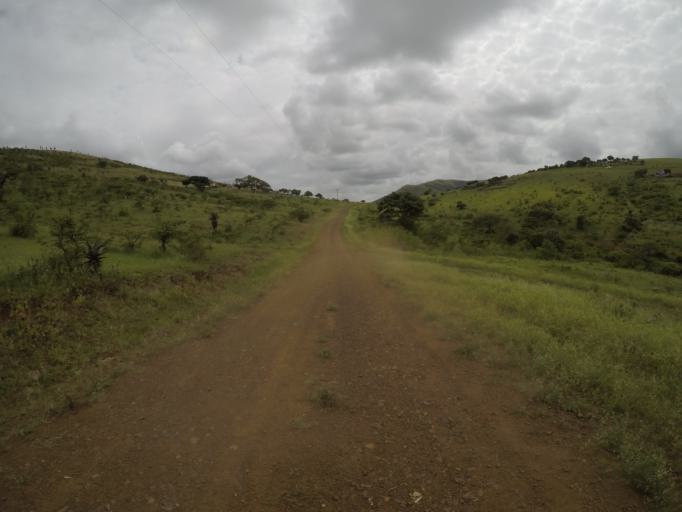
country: ZA
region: KwaZulu-Natal
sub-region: uThungulu District Municipality
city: Empangeni
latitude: -28.6208
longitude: 31.8913
